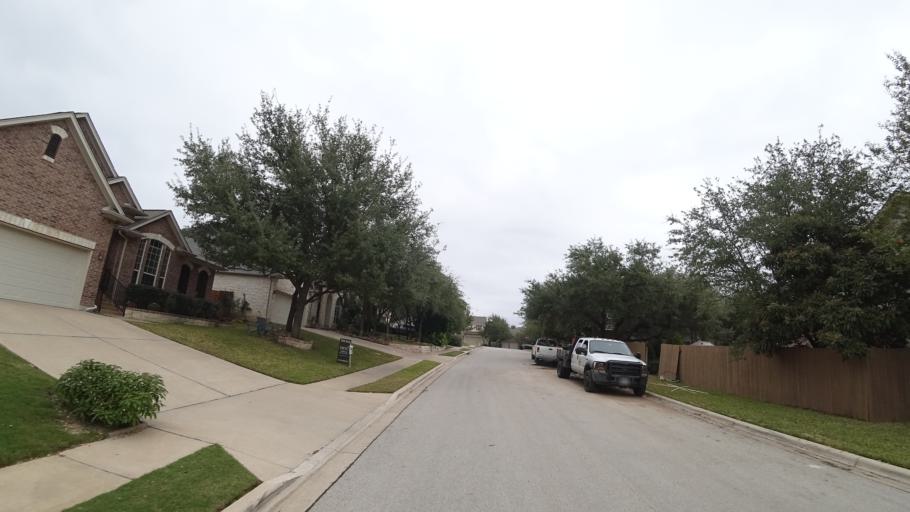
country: US
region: Texas
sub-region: Travis County
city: Bee Cave
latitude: 30.3562
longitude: -97.9070
